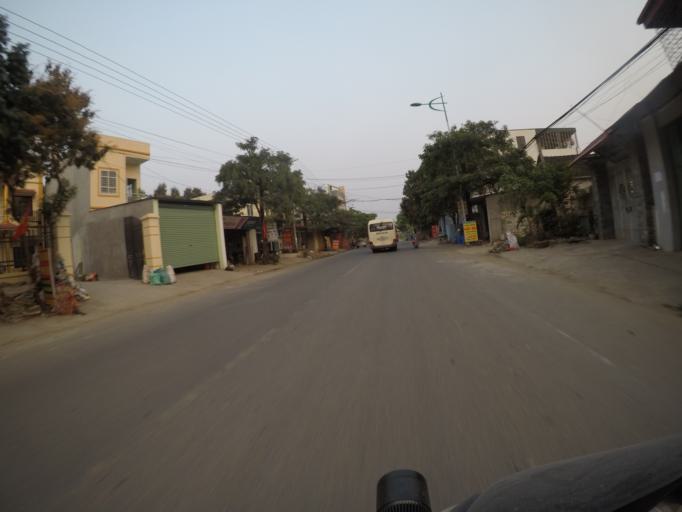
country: VN
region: Vinh Phuc
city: Trai Ngau
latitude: 21.4244
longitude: 105.5950
